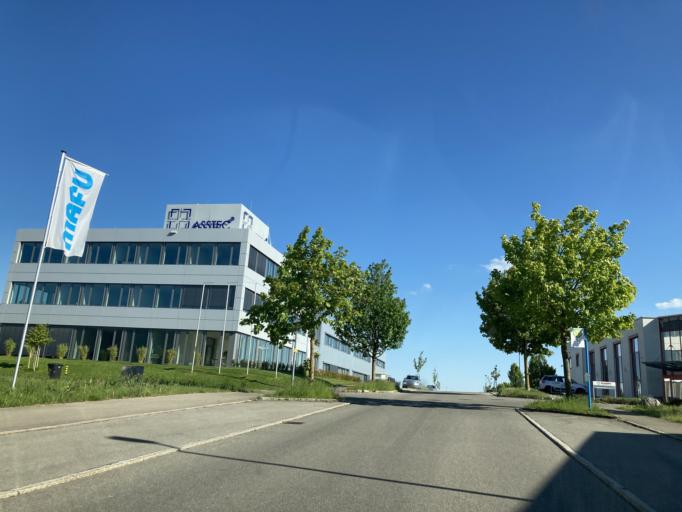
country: DE
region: Baden-Wuerttemberg
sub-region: Freiburg Region
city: Zimmern ob Rottweil
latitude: 48.1671
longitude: 8.5657
